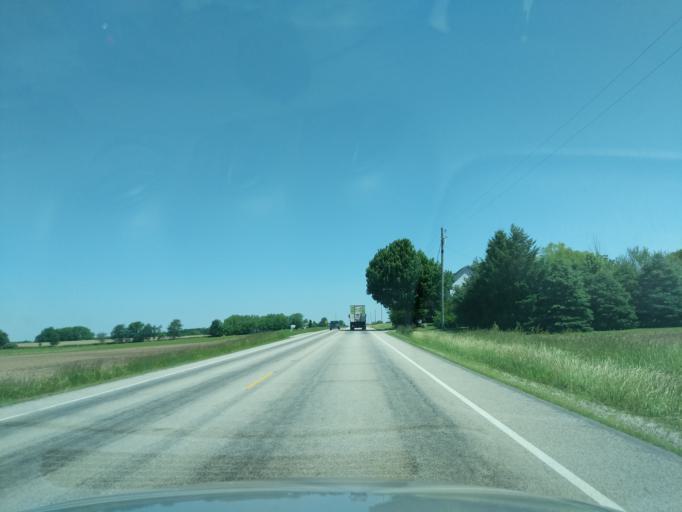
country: US
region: Indiana
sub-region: Huntington County
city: Huntington
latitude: 40.9766
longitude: -85.4714
